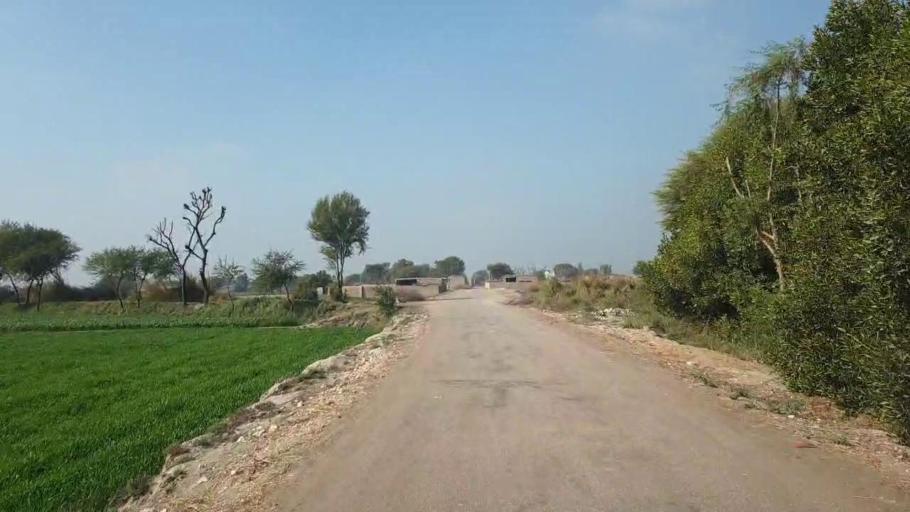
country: PK
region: Sindh
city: Shahdadpur
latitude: 26.0164
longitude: 68.5959
